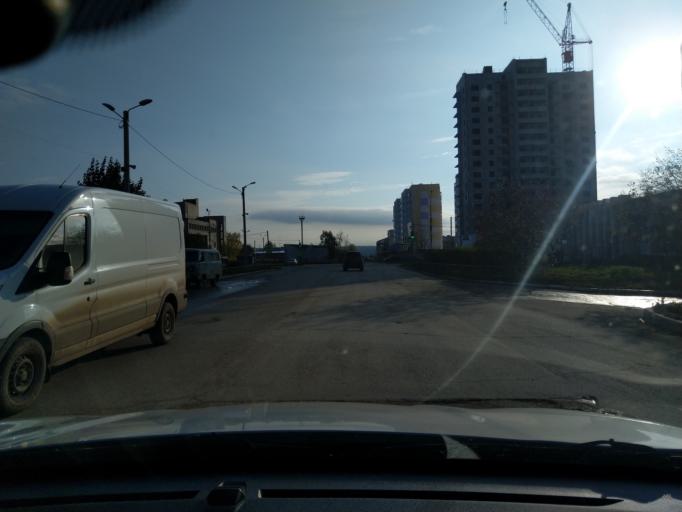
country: RU
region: Perm
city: Dobryanka
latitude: 58.4637
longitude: 56.4005
